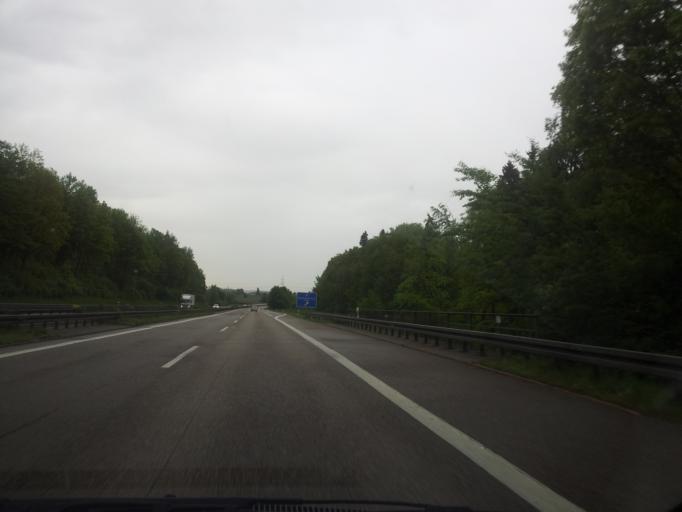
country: DE
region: Bavaria
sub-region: Swabia
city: Bellenberg
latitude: 48.2720
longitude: 10.1137
